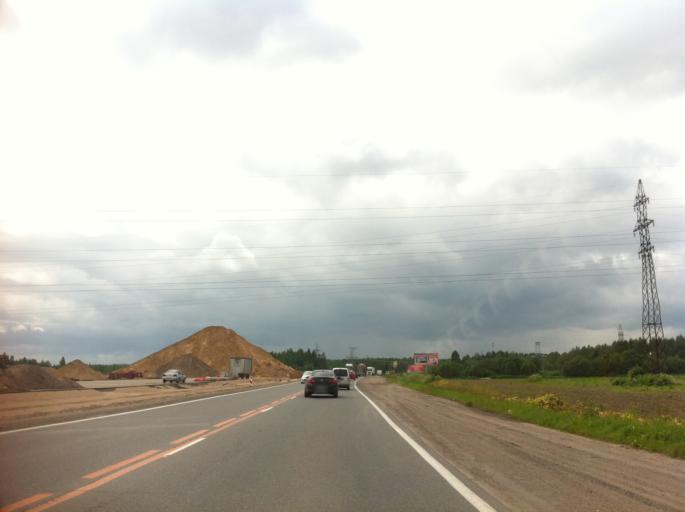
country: RU
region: Leningrad
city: Gatchina
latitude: 59.5299
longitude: 30.1427
